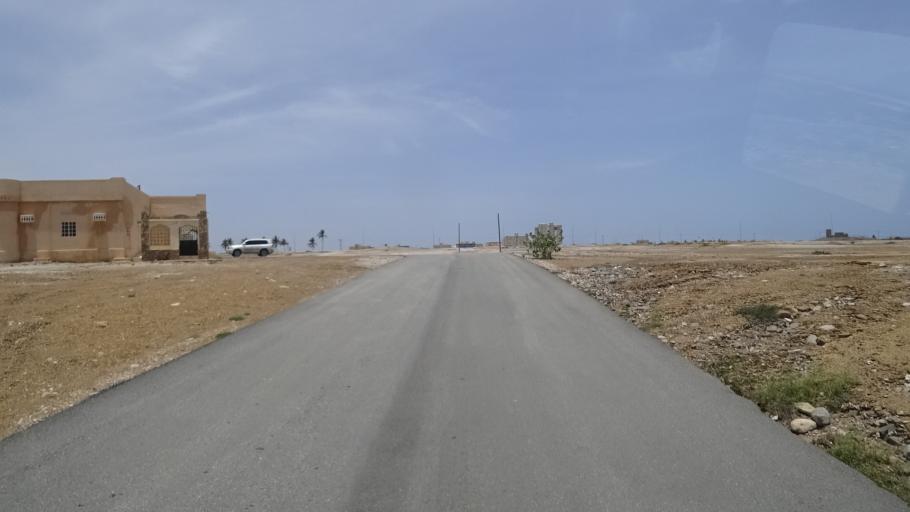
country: OM
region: Zufar
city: Salalah
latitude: 16.9988
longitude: 54.6926
